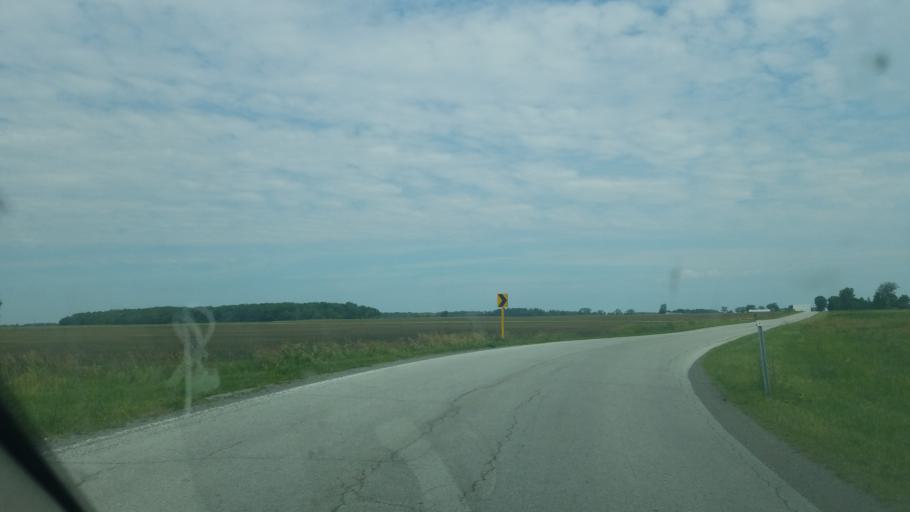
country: US
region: Ohio
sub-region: Seneca County
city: Fostoria
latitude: 41.0794
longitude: -83.4783
